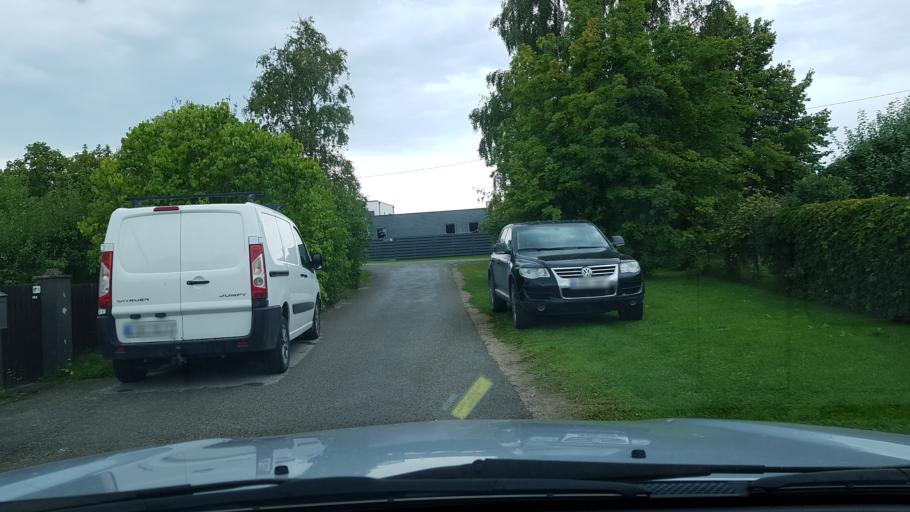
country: EE
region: Harju
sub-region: Rae vald
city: Jueri
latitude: 59.3521
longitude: 24.9047
